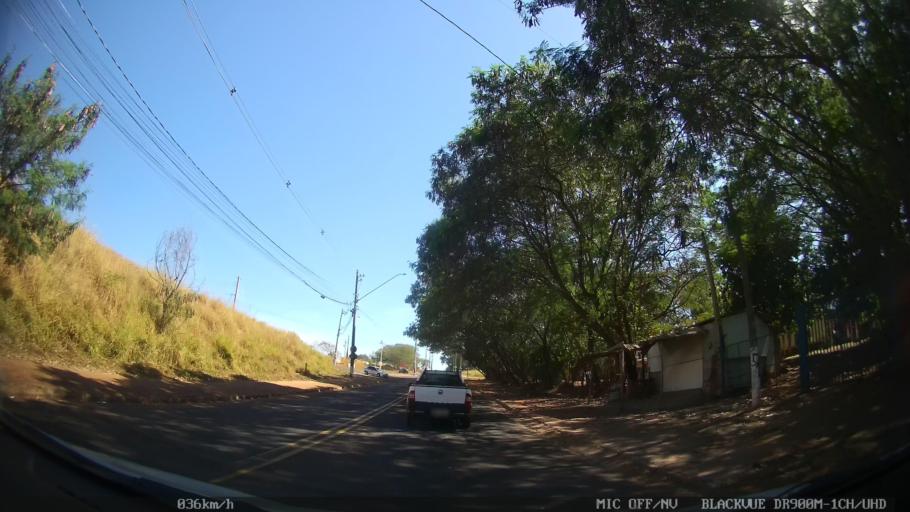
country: BR
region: Sao Paulo
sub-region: Sao Jose Do Rio Preto
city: Sao Jose do Rio Preto
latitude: -20.7646
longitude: -49.4259
